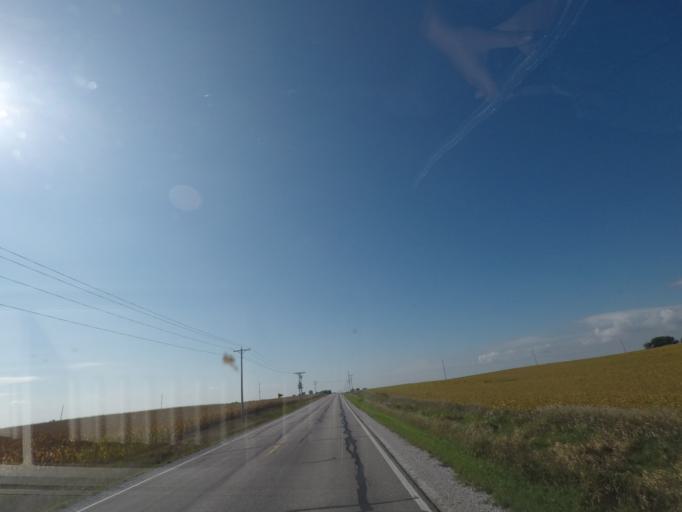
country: US
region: Iowa
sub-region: Story County
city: Nevada
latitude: 42.0371
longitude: -93.4060
